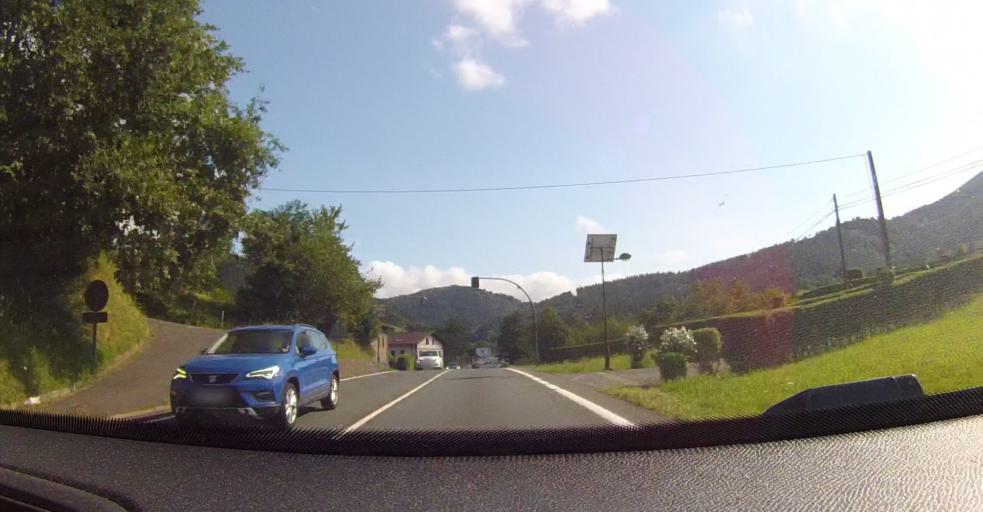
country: ES
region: Basque Country
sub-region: Bizkaia
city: Muxika
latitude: 43.2734
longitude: -2.6851
